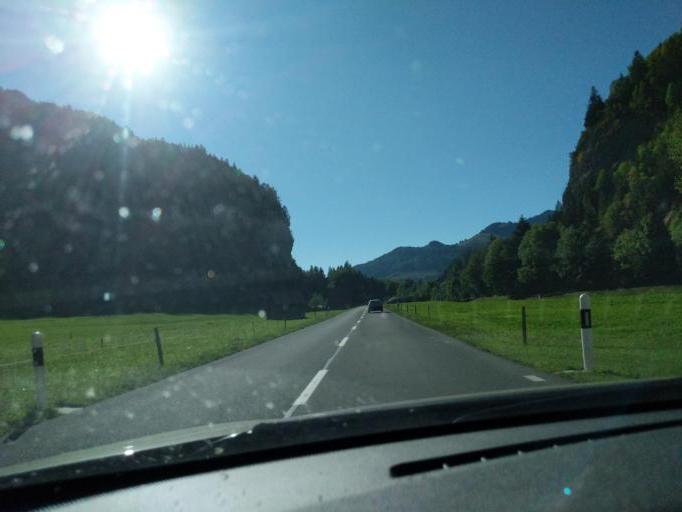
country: CH
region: Fribourg
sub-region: Gruyere District
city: Charmey
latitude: 46.6095
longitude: 7.1856
